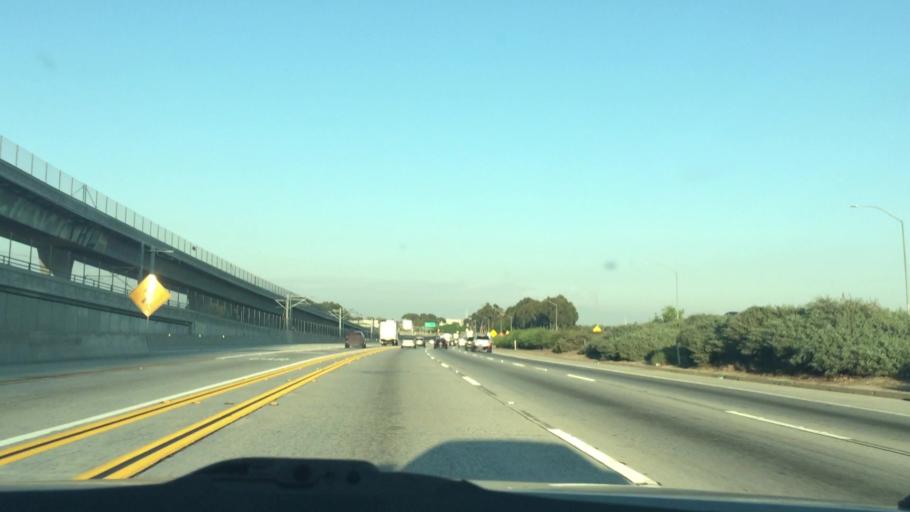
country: US
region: California
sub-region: Los Angeles County
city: Willowbrook
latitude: 33.9281
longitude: -118.2767
